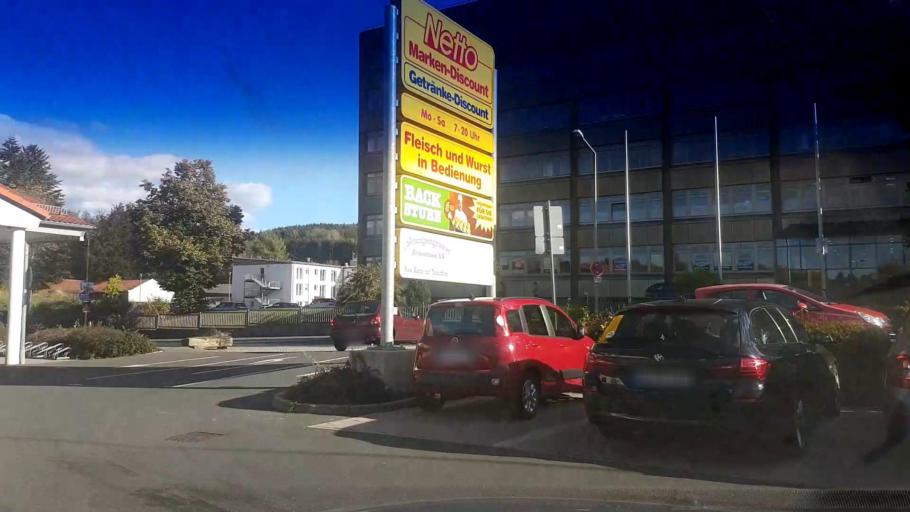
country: DE
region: Bavaria
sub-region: Upper Franconia
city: Gefrees
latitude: 50.0935
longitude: 11.7288
